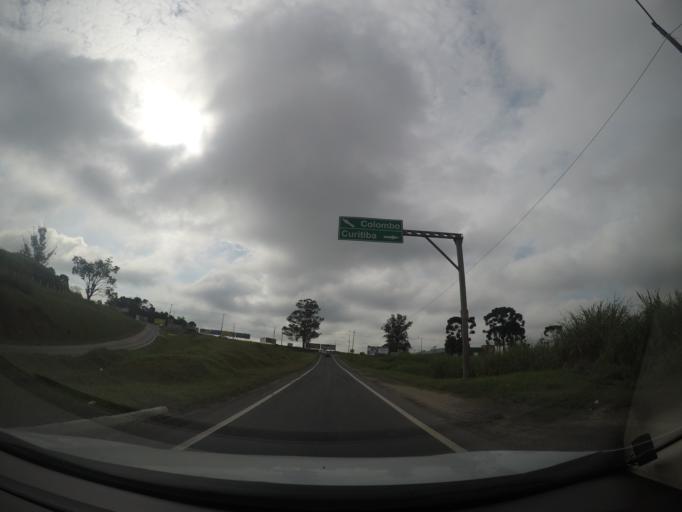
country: BR
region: Parana
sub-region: Colombo
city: Colombo
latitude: -25.3431
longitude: -49.2204
